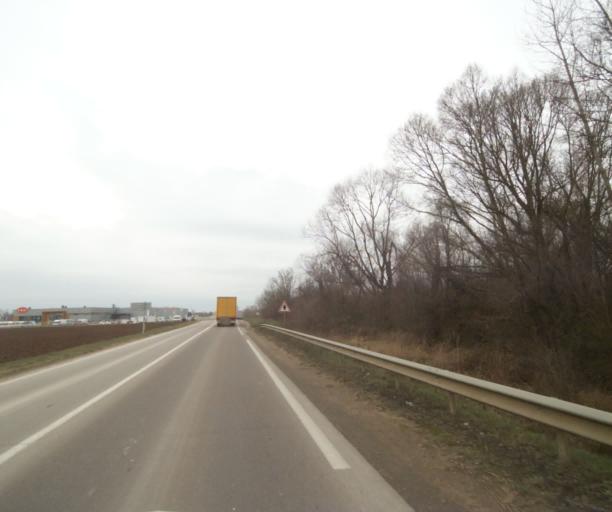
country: FR
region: Champagne-Ardenne
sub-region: Departement de la Haute-Marne
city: Villiers-en-Lieu
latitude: 48.6426
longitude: 4.9144
